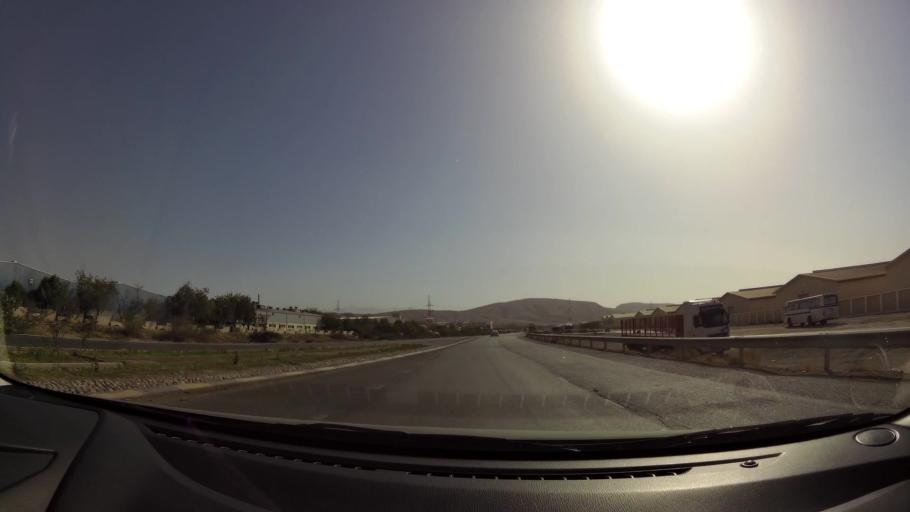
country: OM
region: Muhafazat Masqat
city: As Sib al Jadidah
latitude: 23.5586
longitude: 58.2014
